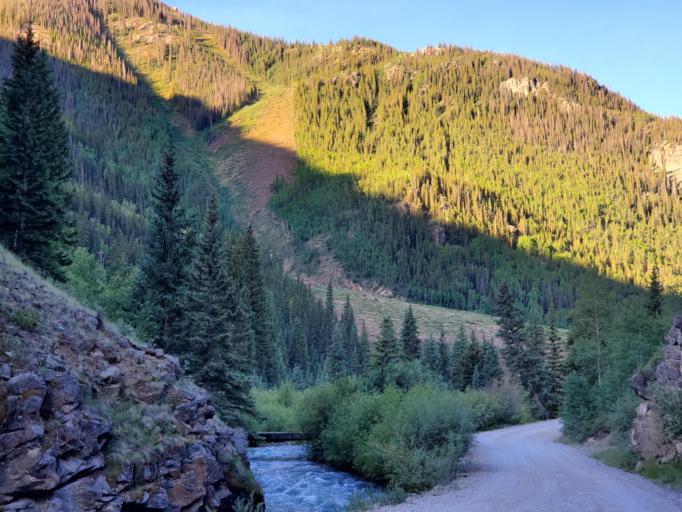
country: US
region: Colorado
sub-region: Hinsdale County
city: Lake City
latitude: 38.0145
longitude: -107.4322
